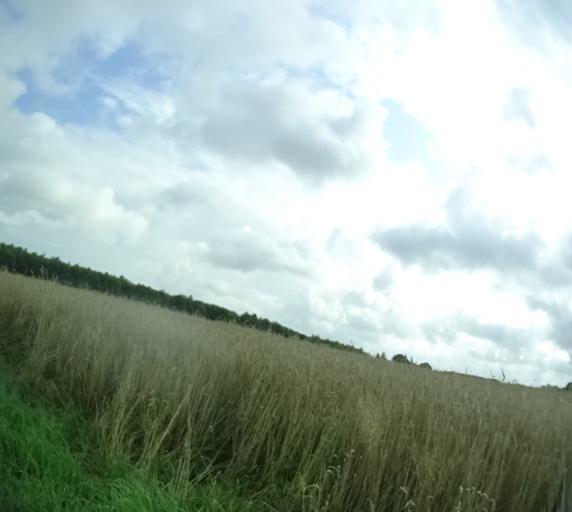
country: DK
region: Central Jutland
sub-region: Syddjurs Kommune
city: Ryomgard
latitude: 56.4000
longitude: 10.4877
